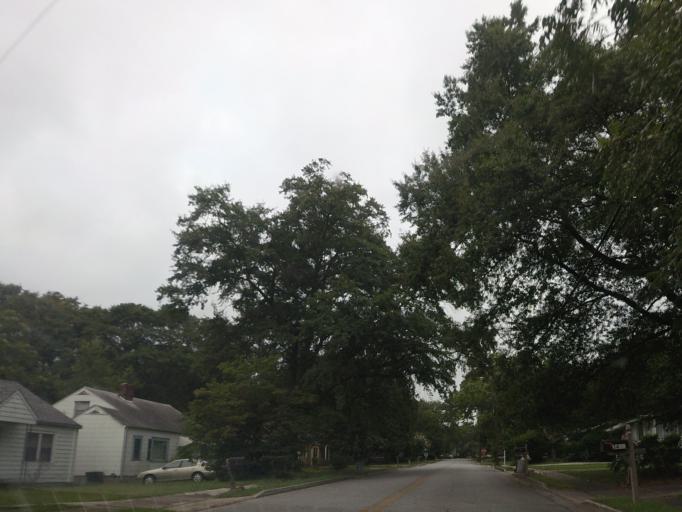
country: US
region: Georgia
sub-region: Fulton County
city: Hapeville
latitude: 33.6596
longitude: -84.4190
